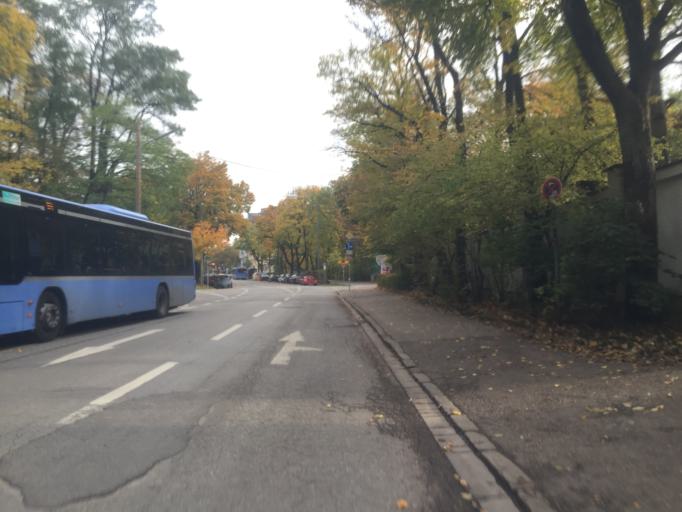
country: DE
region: Bavaria
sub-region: Upper Bavaria
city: Bogenhausen
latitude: 48.1510
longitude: 11.5948
